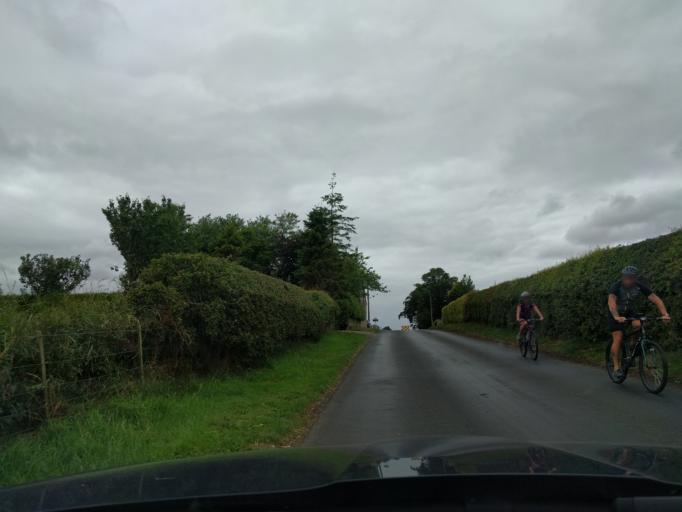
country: GB
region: England
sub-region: Northumberland
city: Berwick-Upon-Tweed
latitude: 55.7508
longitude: -2.0725
